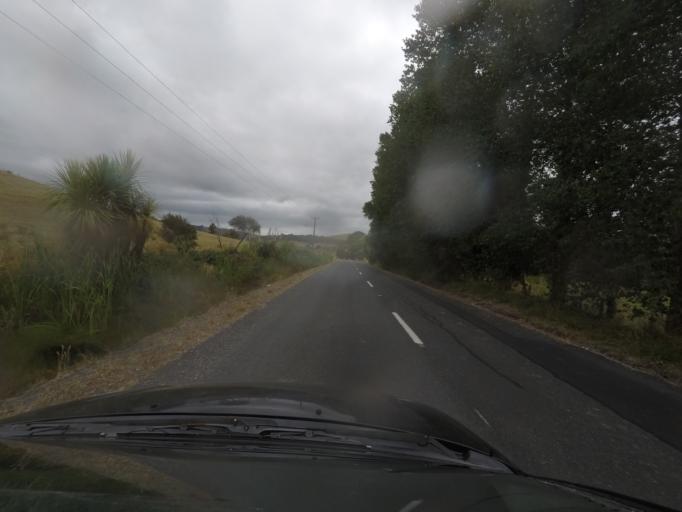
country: NZ
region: Auckland
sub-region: Auckland
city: Warkworth
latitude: -36.2780
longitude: 174.6746
